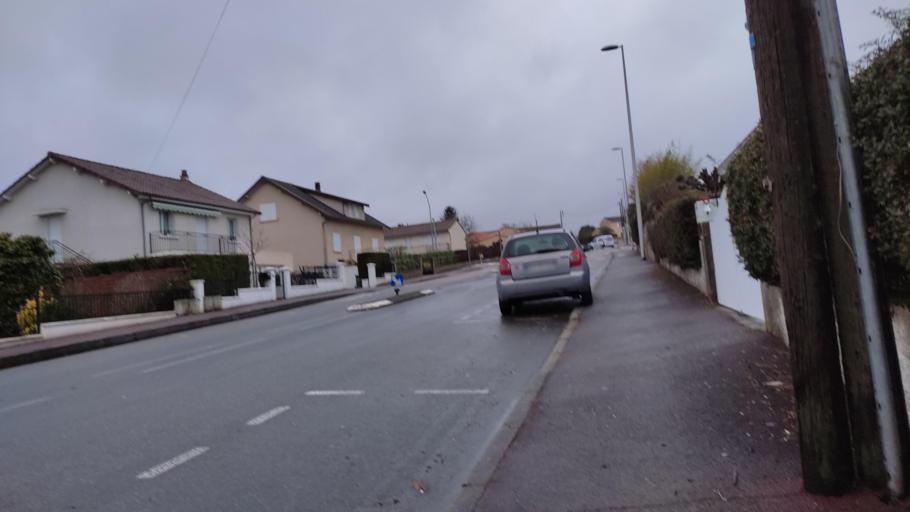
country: FR
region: Limousin
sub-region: Departement de la Haute-Vienne
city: Isle
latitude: 45.8254
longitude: 1.2042
